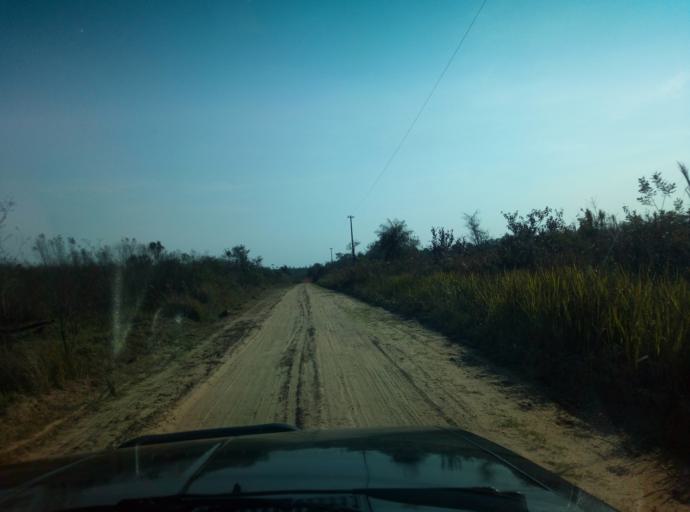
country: PY
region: Caaguazu
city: Doctor Cecilio Baez
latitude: -25.1854
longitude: -56.1919
